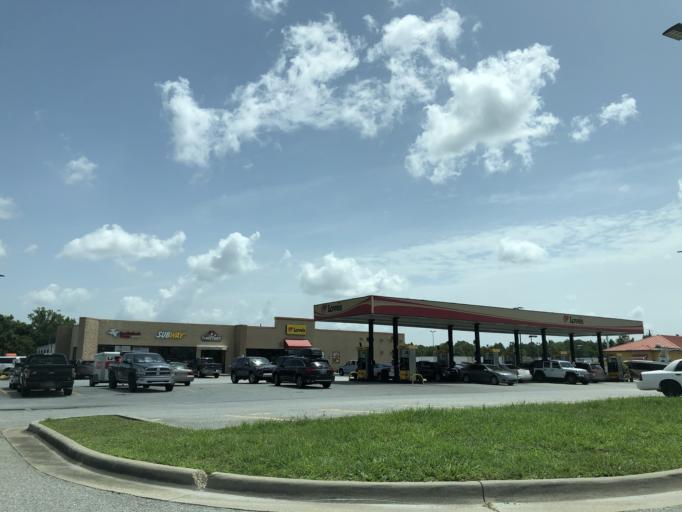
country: US
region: Georgia
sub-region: Glynn County
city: Brunswick
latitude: 31.1373
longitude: -81.5724
